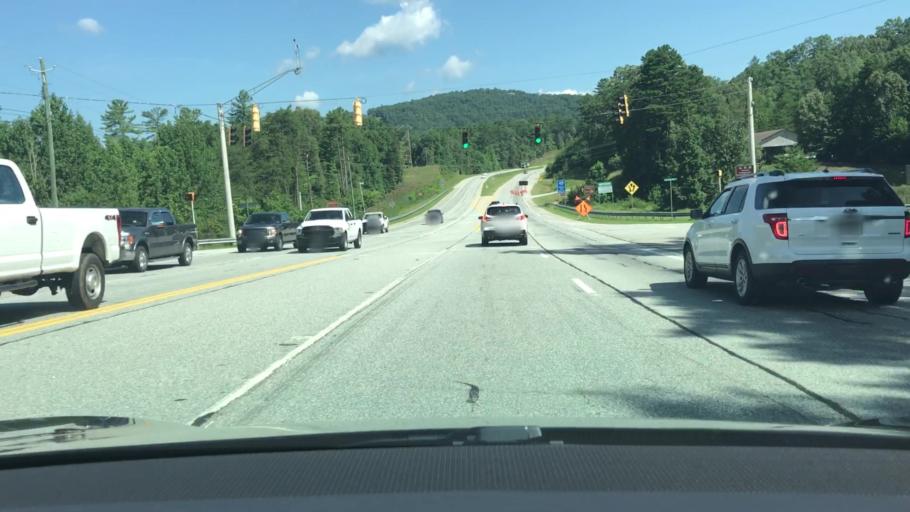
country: US
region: Georgia
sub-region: Rabun County
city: Clayton
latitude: 34.7422
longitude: -83.4003
